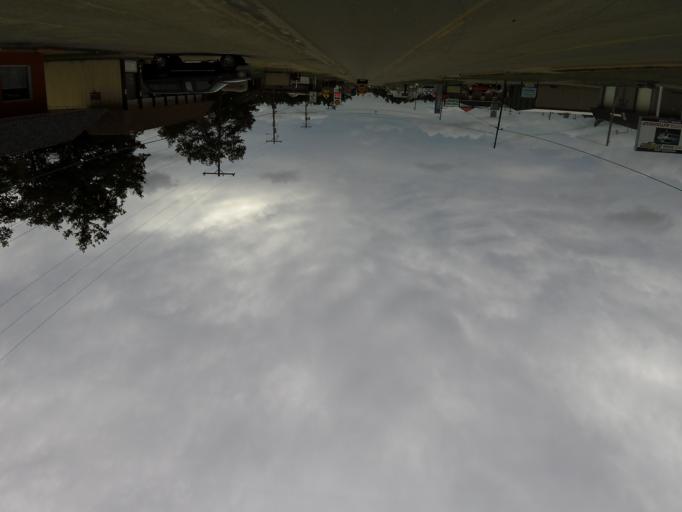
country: US
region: Michigan
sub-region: Roscommon County
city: Saint Helen
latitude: 44.3658
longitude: -84.4103
